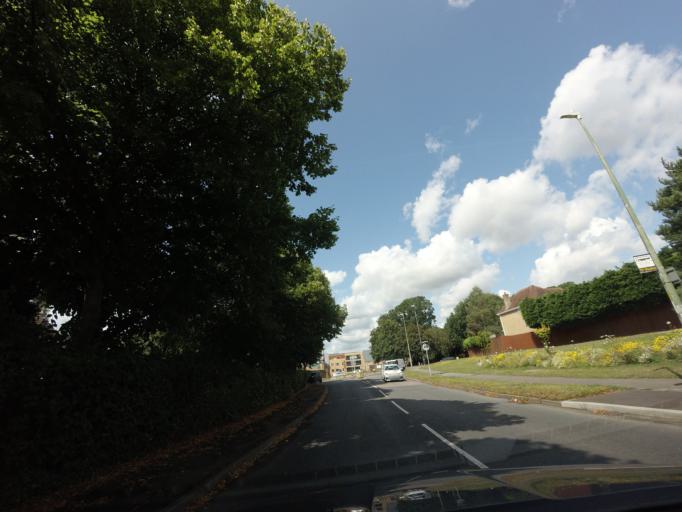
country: GB
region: England
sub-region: Kent
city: Boxley
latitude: 51.2790
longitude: 0.5520
